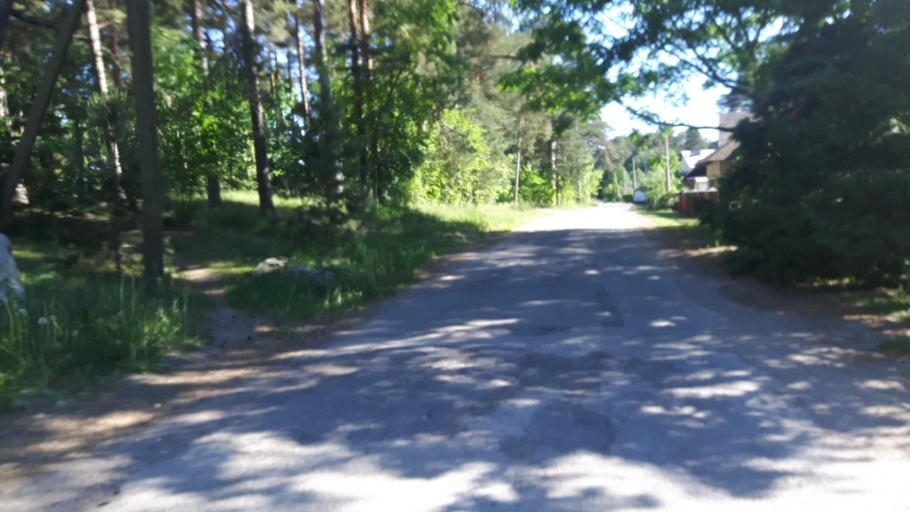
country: LV
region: Salacgrivas
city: Salacgriva
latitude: 57.7458
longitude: 24.3531
